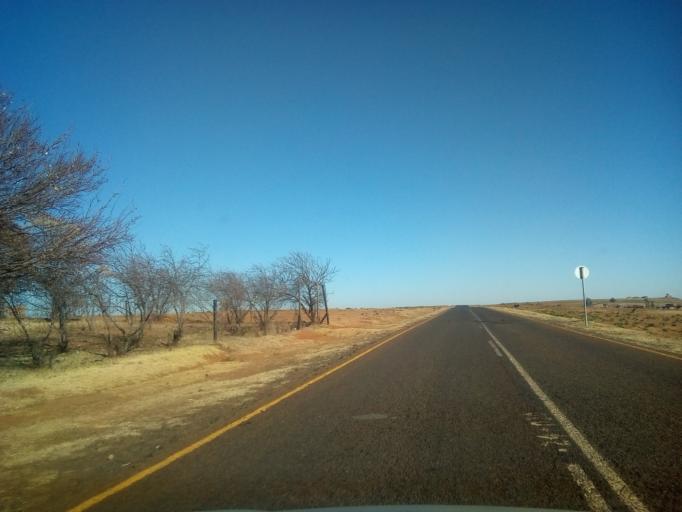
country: LS
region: Berea
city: Teyateyaneng
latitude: -29.2570
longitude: 27.7549
